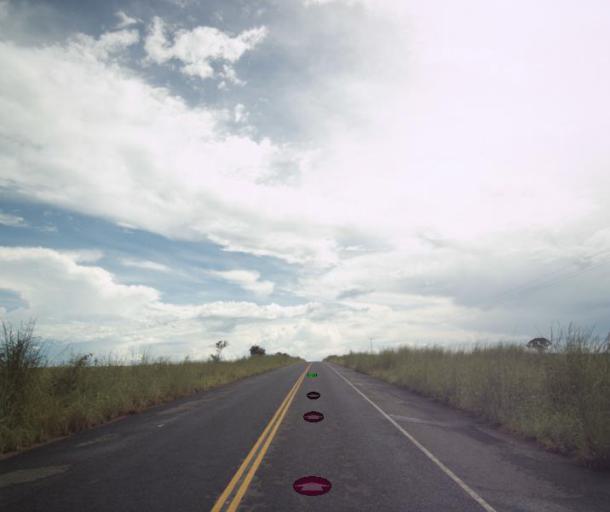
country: BR
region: Goias
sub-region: Sao Miguel Do Araguaia
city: Sao Miguel do Araguaia
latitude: -13.2912
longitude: -50.2144
